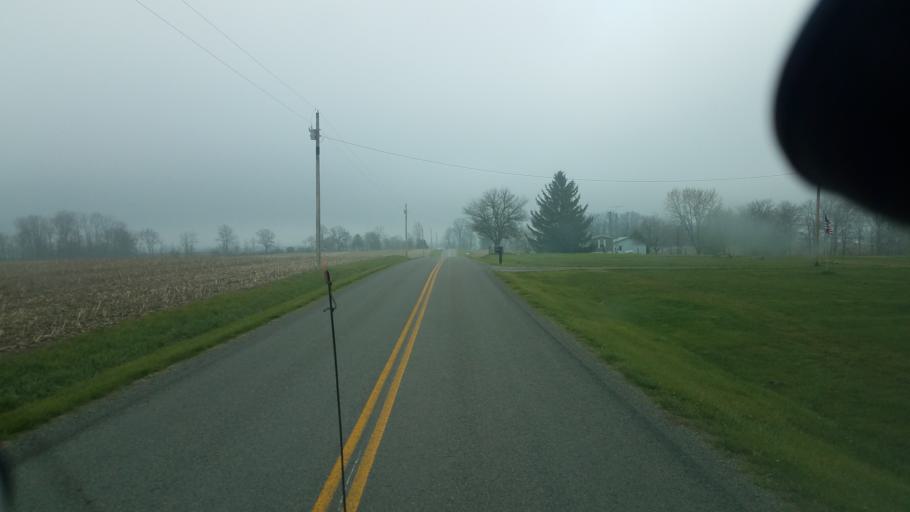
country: US
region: Ohio
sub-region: Logan County
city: Bellefontaine
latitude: 40.4053
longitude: -83.8221
